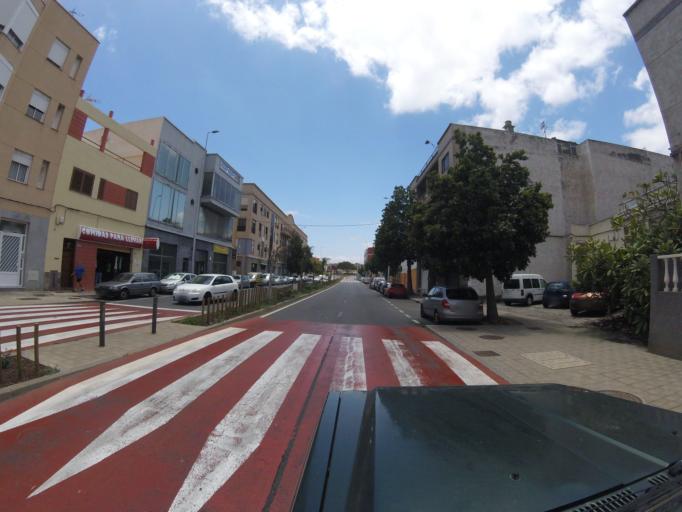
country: ES
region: Canary Islands
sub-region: Provincia de Santa Cruz de Tenerife
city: La Laguna
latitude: 28.4424
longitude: -16.3019
